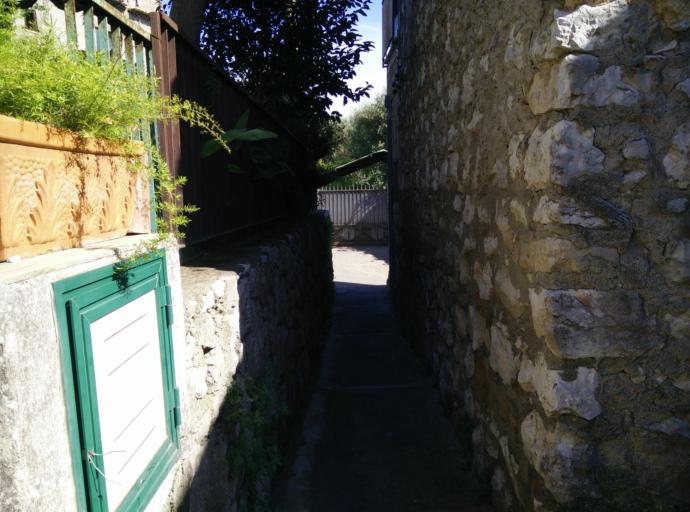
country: IT
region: Campania
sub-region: Provincia di Napoli
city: Massa Lubrense
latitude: 40.5999
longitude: 14.3829
